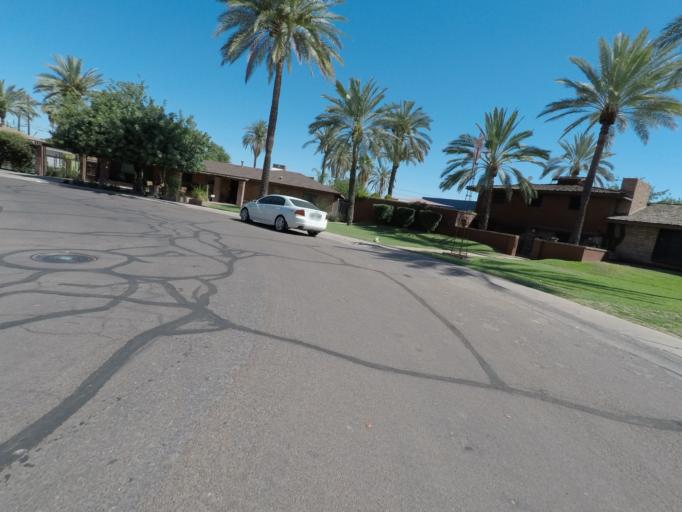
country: US
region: Arizona
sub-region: Maricopa County
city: Tempe Junction
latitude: 33.4065
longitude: -111.9413
